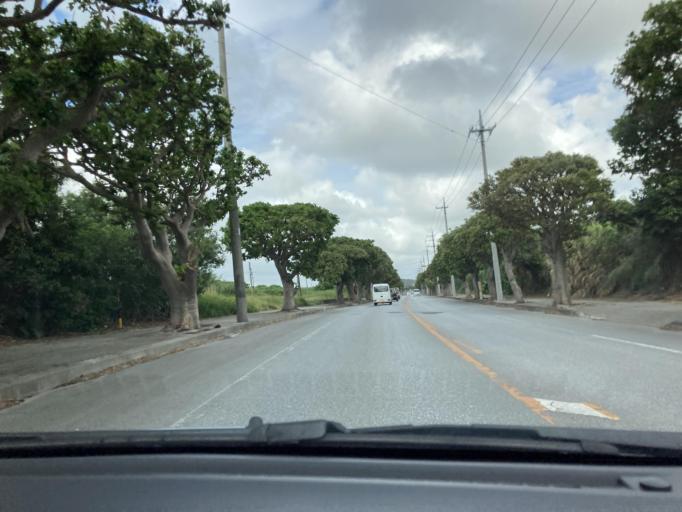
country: JP
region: Okinawa
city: Itoman
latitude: 26.1384
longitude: 127.6887
